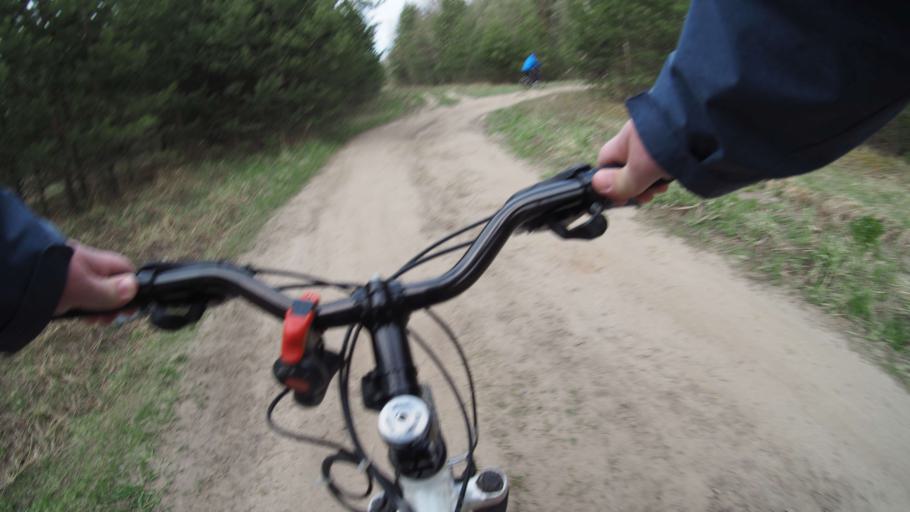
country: RU
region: Moskovskaya
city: Ramenskoye
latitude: 55.5917
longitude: 38.2898
